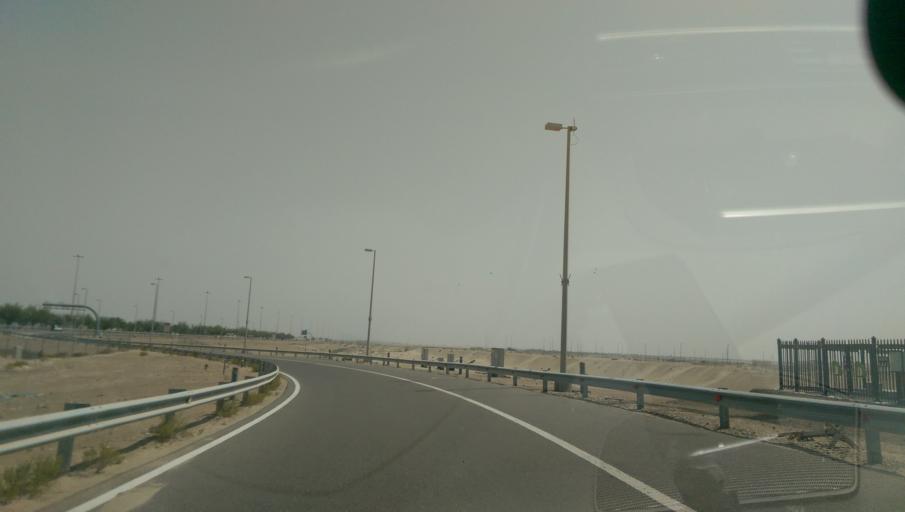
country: AE
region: Abu Dhabi
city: Abu Dhabi
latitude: 24.3885
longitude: 54.6647
